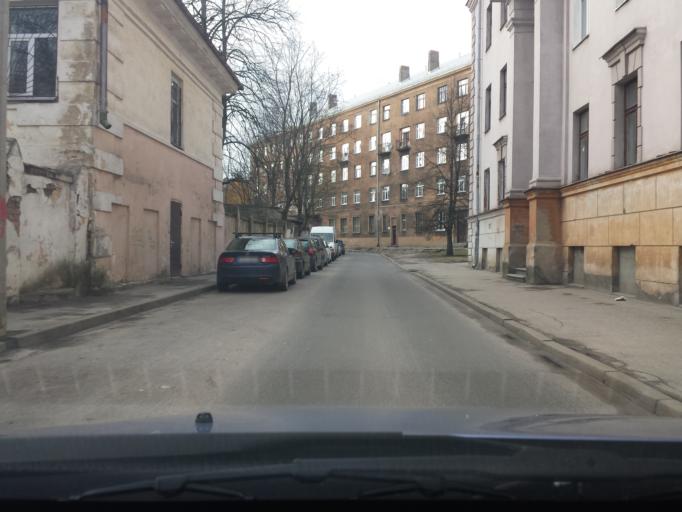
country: LV
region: Riga
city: Riga
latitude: 56.9960
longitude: 24.1235
